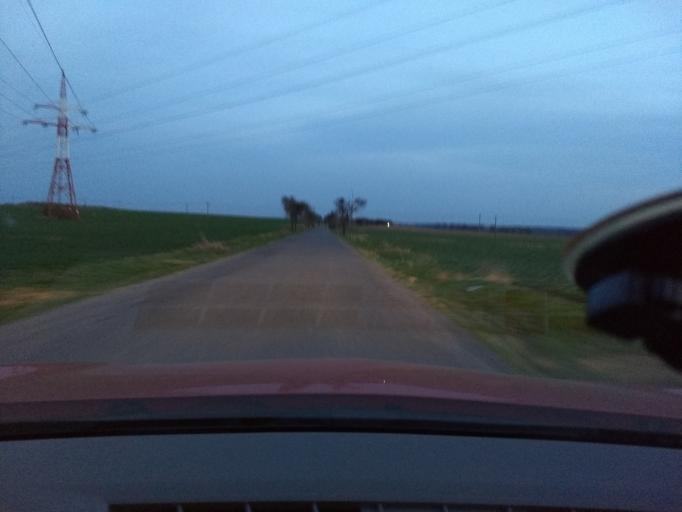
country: CZ
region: Central Bohemia
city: Jenec
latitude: 50.0613
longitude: 14.1869
